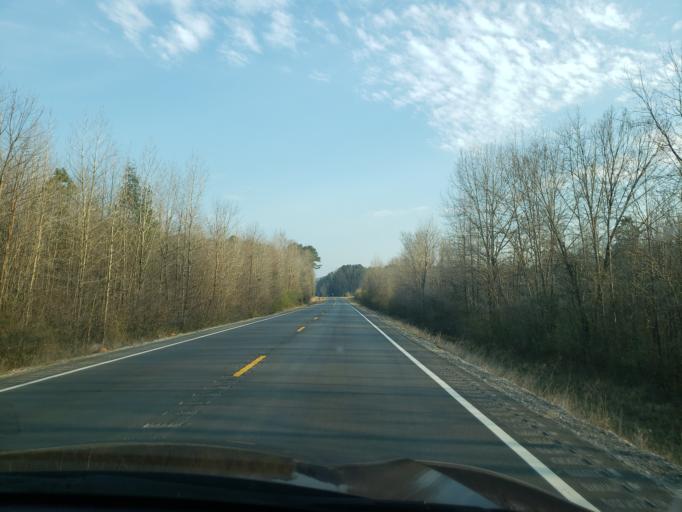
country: US
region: Alabama
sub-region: Hale County
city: Greensboro
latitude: 32.8270
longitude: -87.6032
